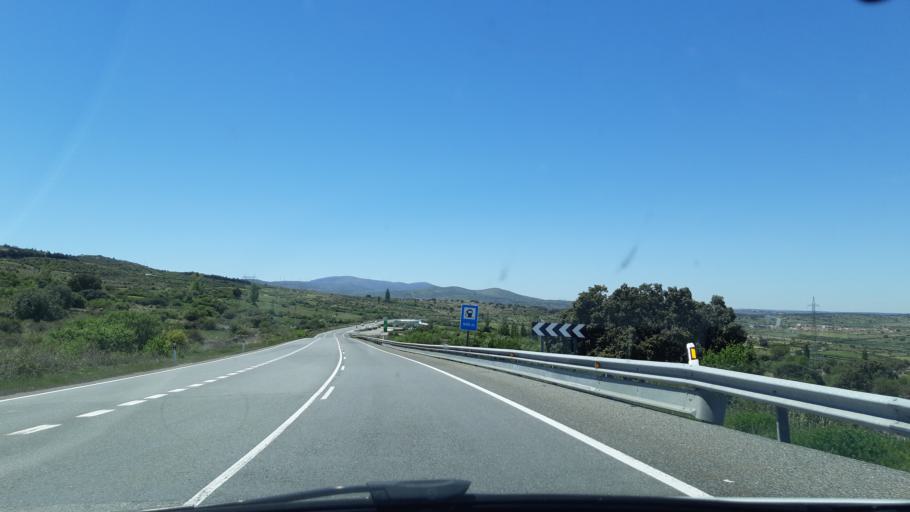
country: ES
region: Castille and Leon
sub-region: Provincia de Segovia
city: Vegas de Matute
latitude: 40.7501
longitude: -4.2927
